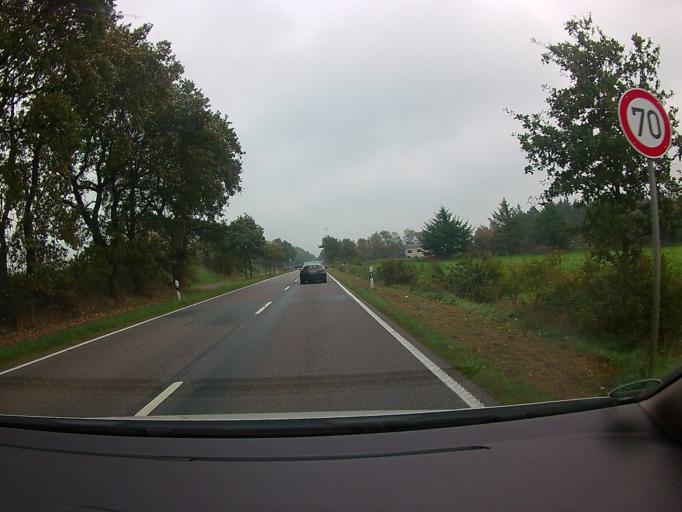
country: DE
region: Schleswig-Holstein
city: Goldebek
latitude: 54.6761
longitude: 9.1413
